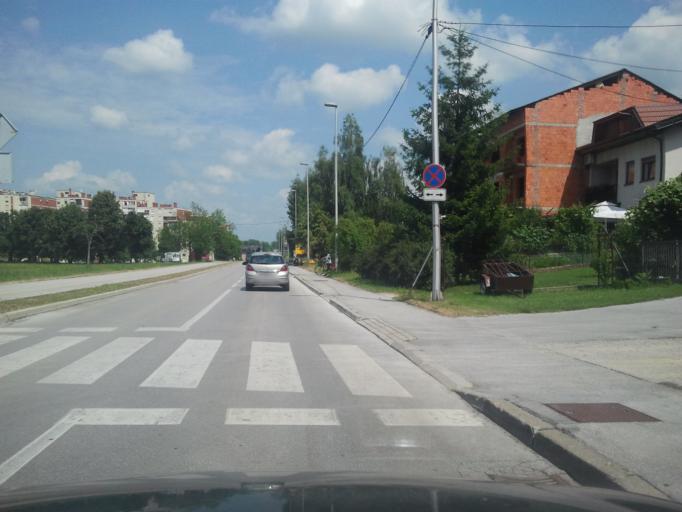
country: HR
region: Karlovacka
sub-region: Grad Karlovac
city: Karlovac
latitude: 45.4797
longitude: 15.5495
